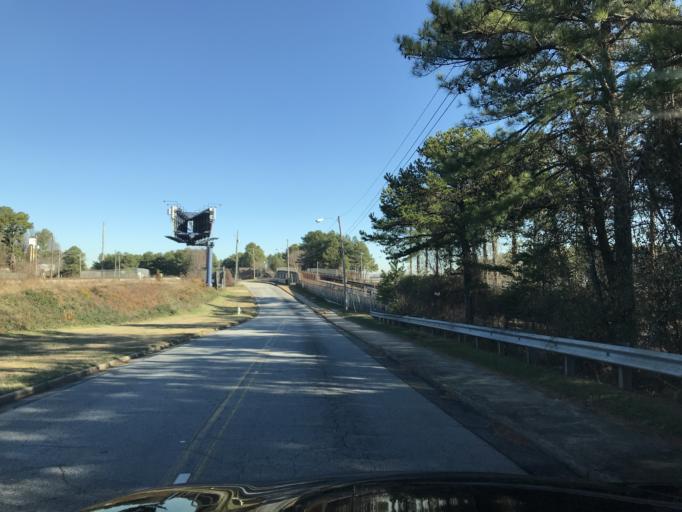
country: US
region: Georgia
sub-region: Fulton County
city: College Park
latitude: 33.6443
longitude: -84.4518
